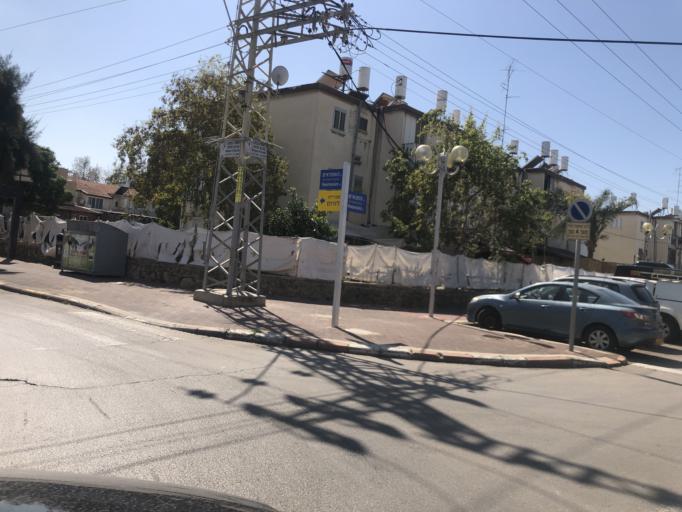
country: IL
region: Tel Aviv
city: Holon
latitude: 32.0059
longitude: 34.7631
